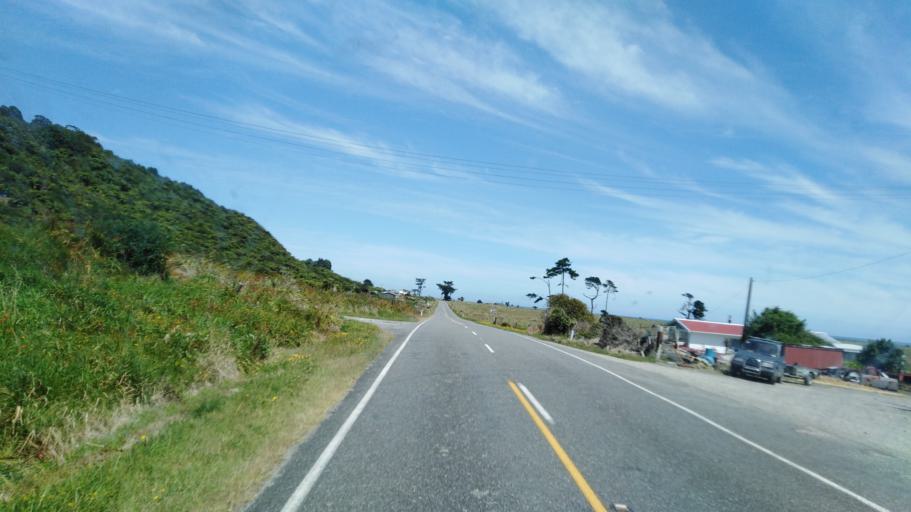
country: NZ
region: West Coast
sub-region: Buller District
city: Westport
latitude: -41.5337
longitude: 171.9363
